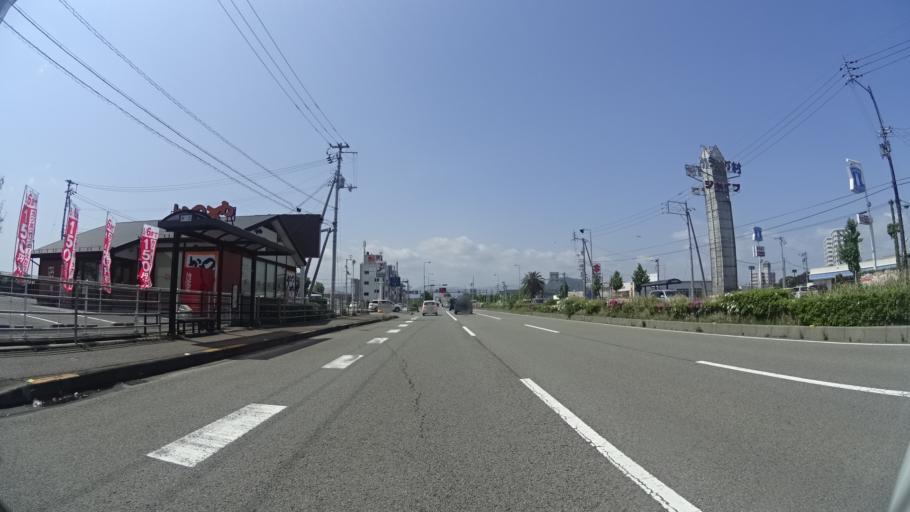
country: JP
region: Tokushima
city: Tokushima-shi
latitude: 34.0978
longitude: 134.5737
